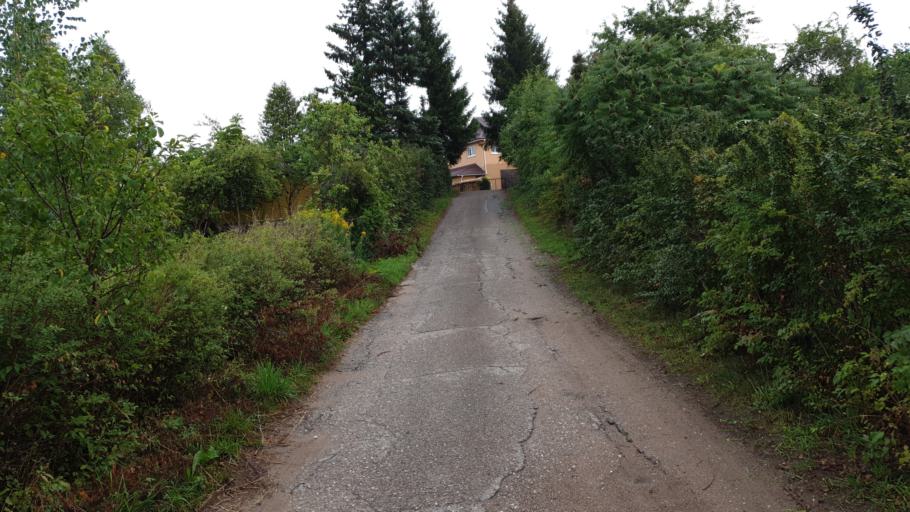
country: LT
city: Grigiskes
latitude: 54.7668
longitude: 25.0168
